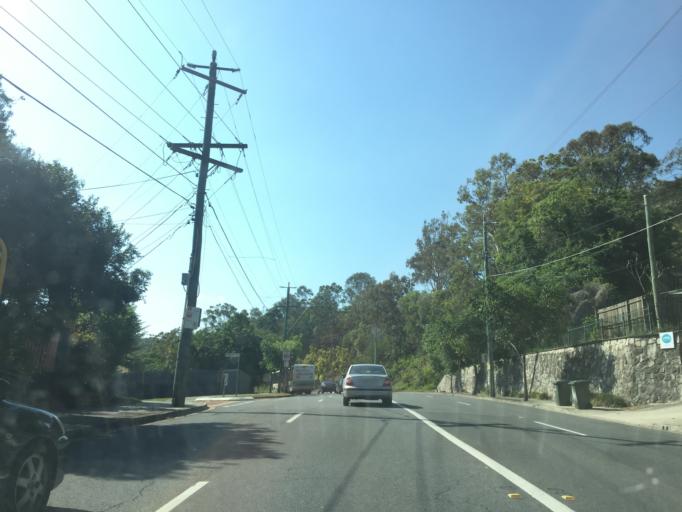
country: AU
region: Queensland
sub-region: Brisbane
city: Toowong
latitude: -27.4481
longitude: 152.9656
